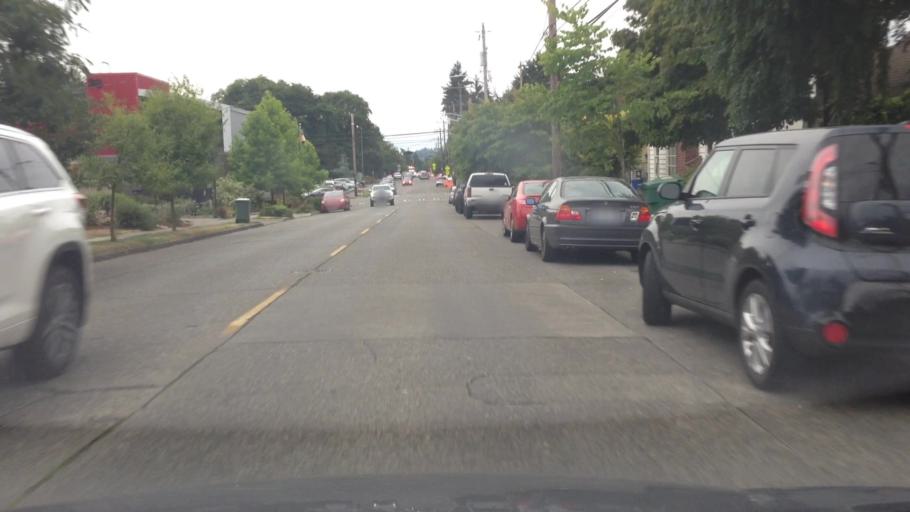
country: US
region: Washington
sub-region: King County
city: Yarrow Point
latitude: 47.6694
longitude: -122.2848
